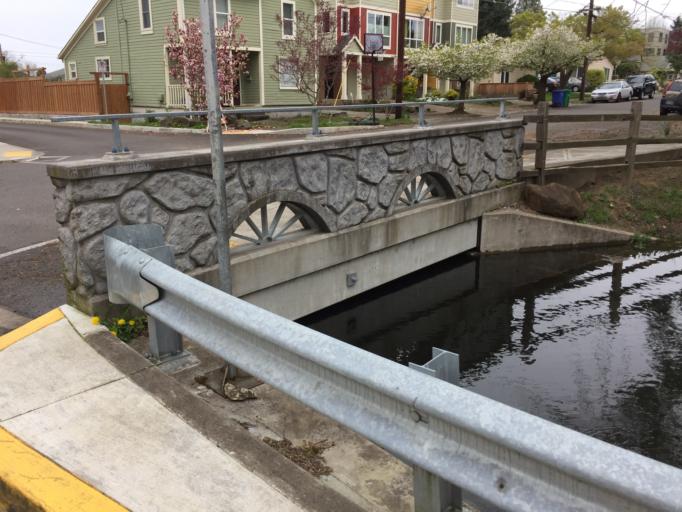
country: US
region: Oregon
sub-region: Clackamas County
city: Milwaukie
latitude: 45.4635
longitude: -122.6432
